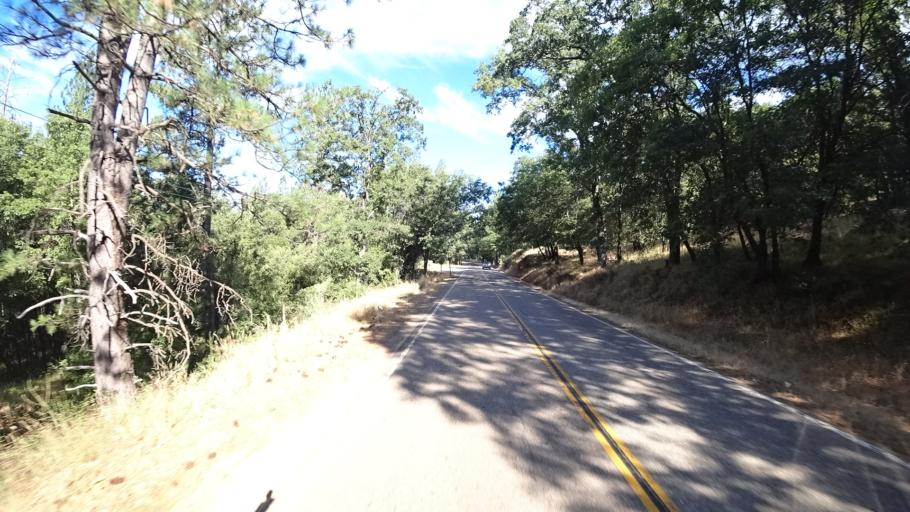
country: US
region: California
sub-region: Amador County
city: Pioneer
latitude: 38.3803
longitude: -120.5210
